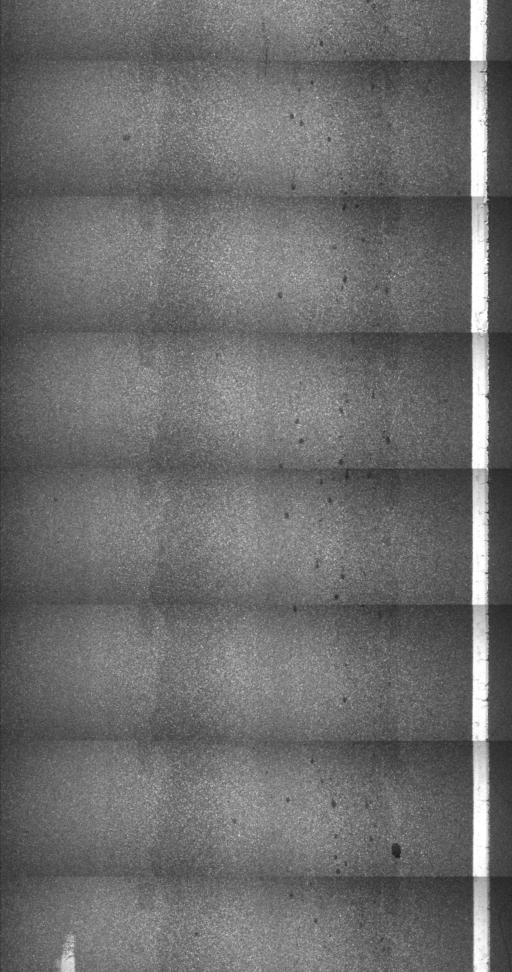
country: US
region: New York
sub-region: Washington County
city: Granville
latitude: 43.3044
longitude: -73.1541
